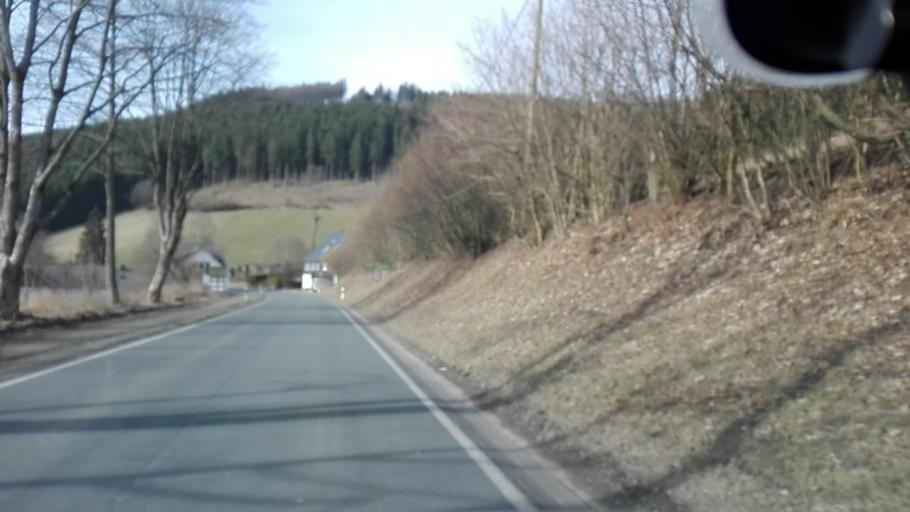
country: DE
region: North Rhine-Westphalia
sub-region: Regierungsbezirk Arnsberg
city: Bad Fredeburg
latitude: 51.1684
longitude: 8.3926
